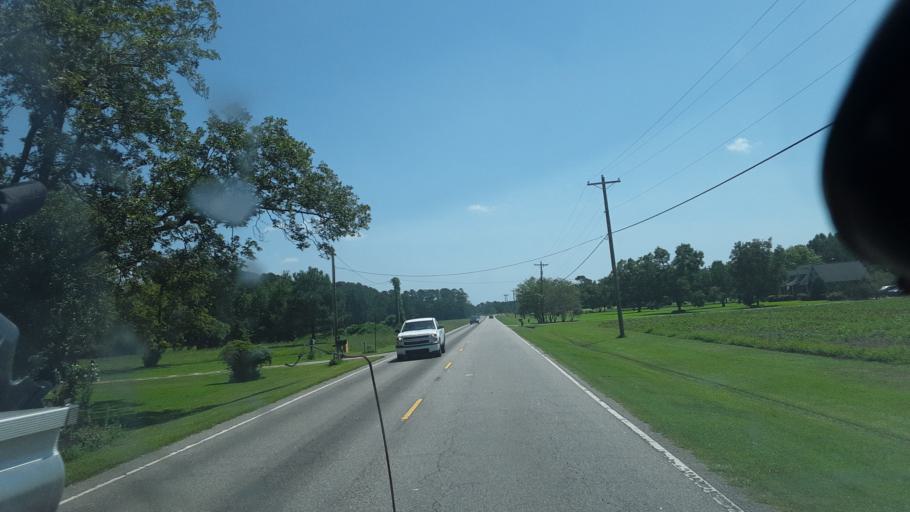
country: US
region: South Carolina
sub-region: Horry County
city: North Myrtle Beach
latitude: 33.8565
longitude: -78.7159
